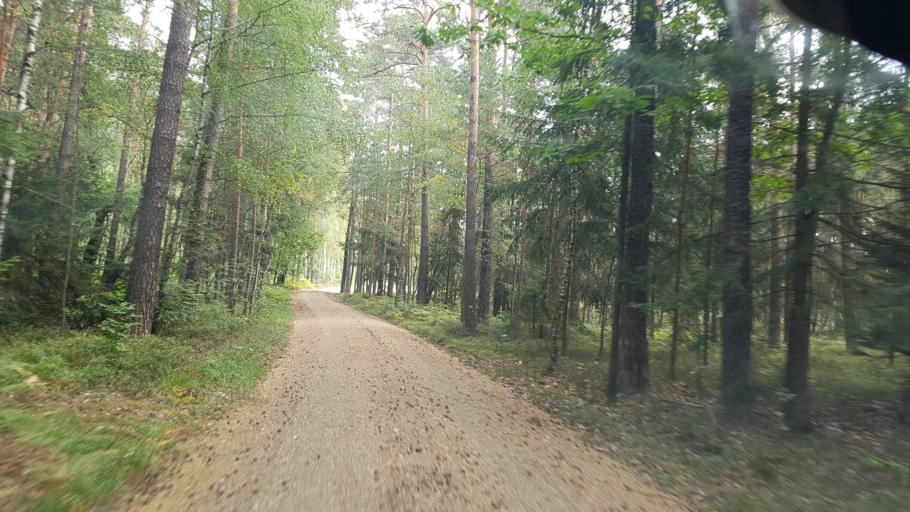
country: DE
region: Brandenburg
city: Ruckersdorf
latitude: 51.5714
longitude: 13.6292
